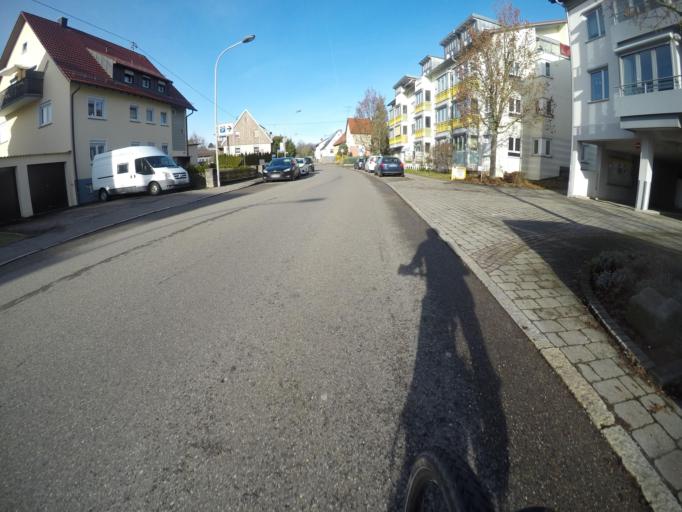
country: DE
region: Baden-Wuerttemberg
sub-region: Regierungsbezirk Stuttgart
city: Korb
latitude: 48.8444
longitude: 9.3586
